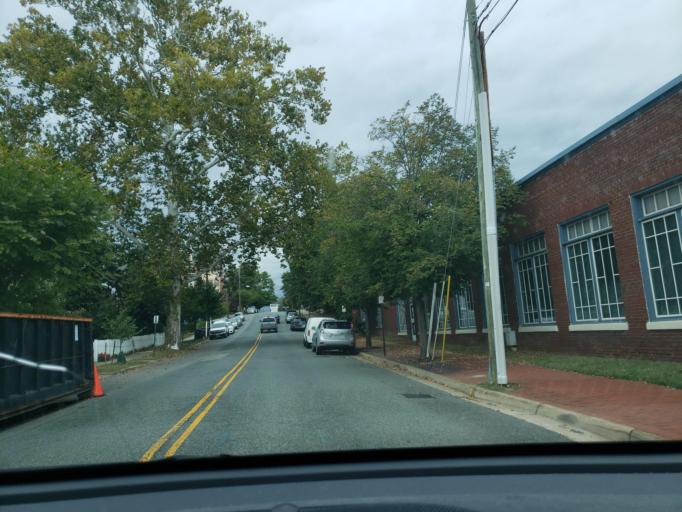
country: US
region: Virginia
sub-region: City of Fredericksburg
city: Fredericksburg
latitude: 38.2987
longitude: -77.4603
